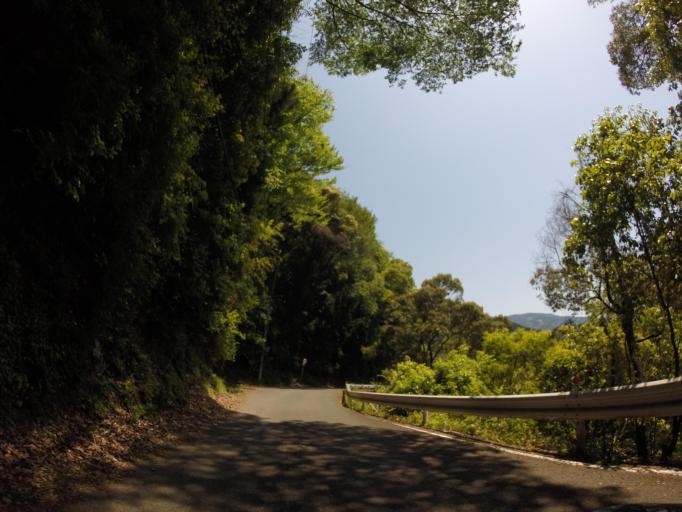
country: JP
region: Shizuoka
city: Shizuoka-shi
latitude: 35.1013
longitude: 138.2322
